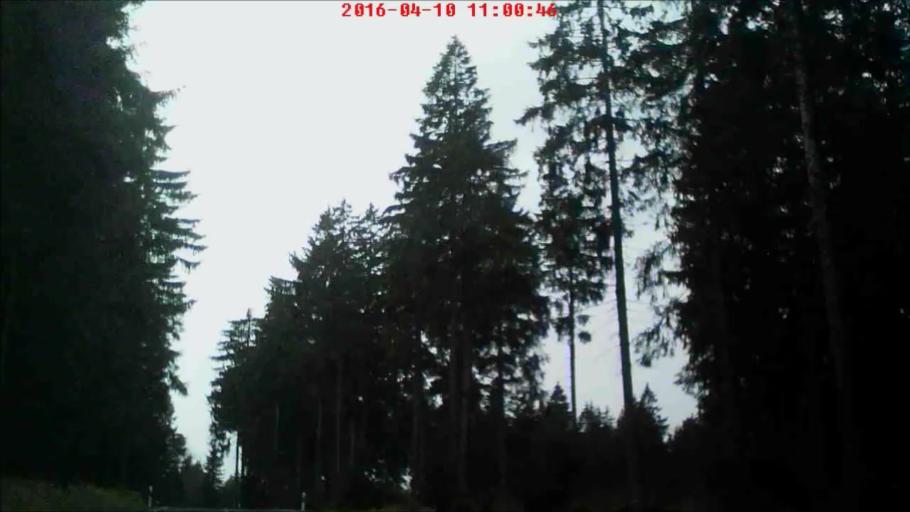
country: DE
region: Thuringia
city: Frauenwald
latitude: 50.6048
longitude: 10.8571
